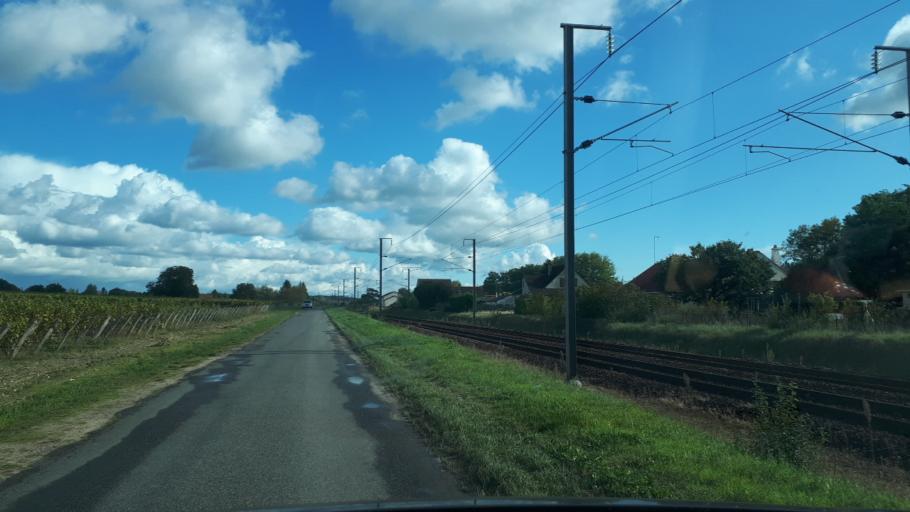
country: FR
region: Centre
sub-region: Departement du Loir-et-Cher
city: Thesee
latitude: 47.3184
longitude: 1.3234
